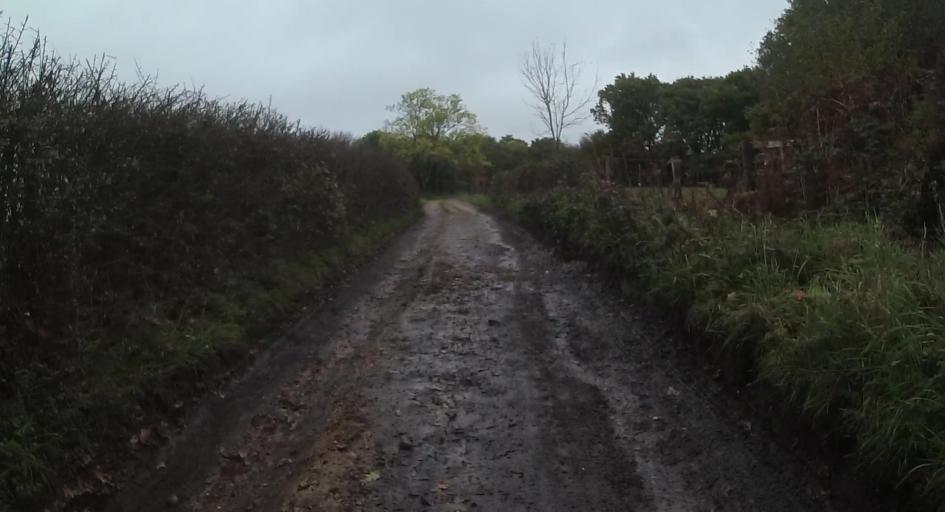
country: GB
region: England
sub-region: Surrey
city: Farnham
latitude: 51.2274
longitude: -0.8156
